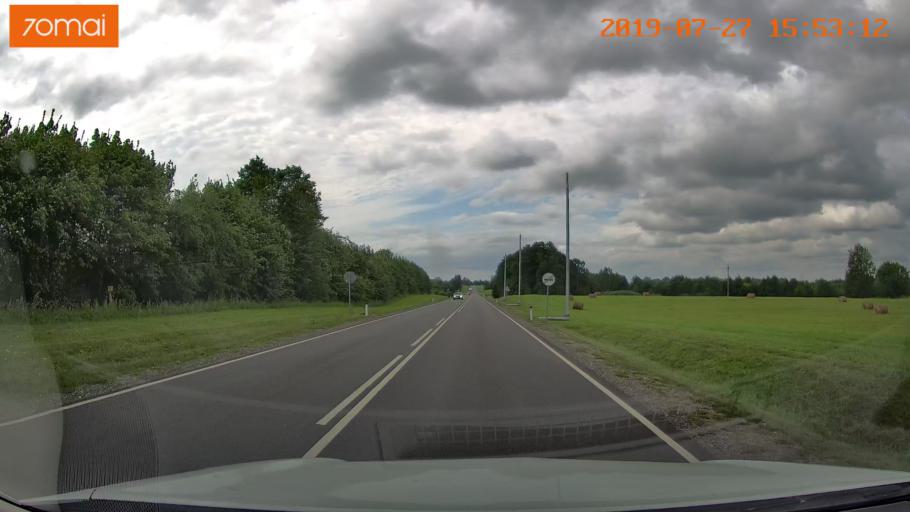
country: RU
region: Kaliningrad
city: Chernyakhovsk
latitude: 54.6027
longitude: 21.9577
